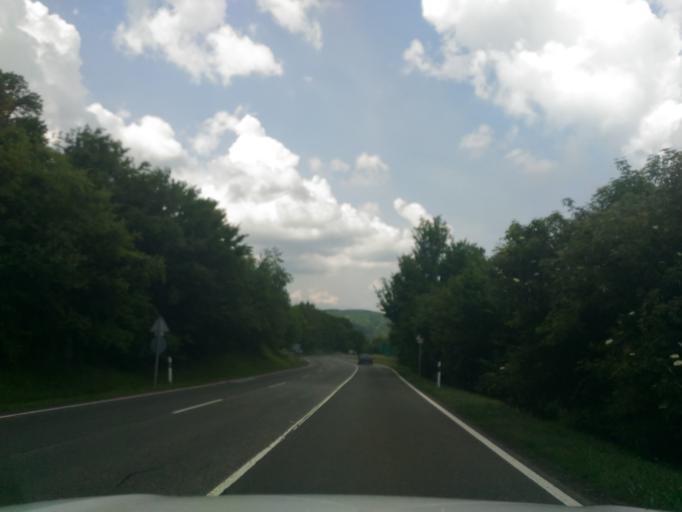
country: HU
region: Baranya
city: Komlo
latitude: 46.1572
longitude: 18.2409
